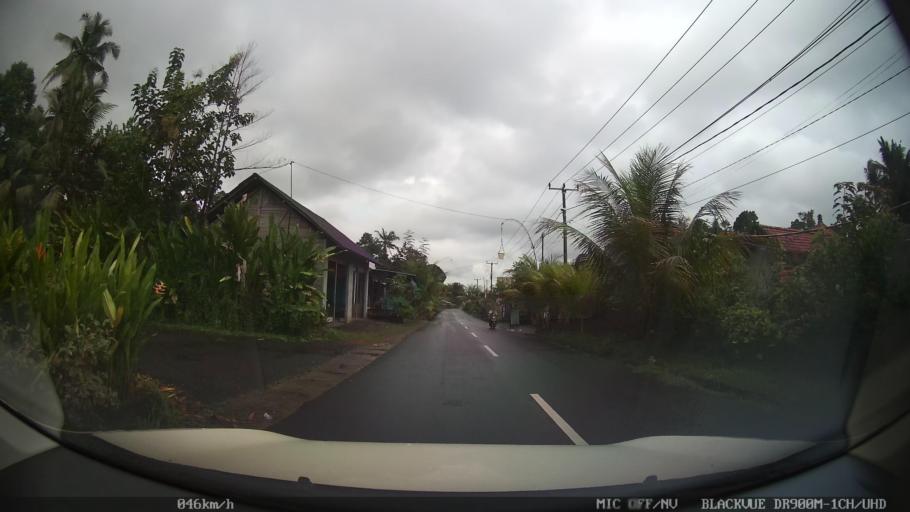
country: ID
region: Bali
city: Banjar Teguan
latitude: -8.4978
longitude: 115.2378
